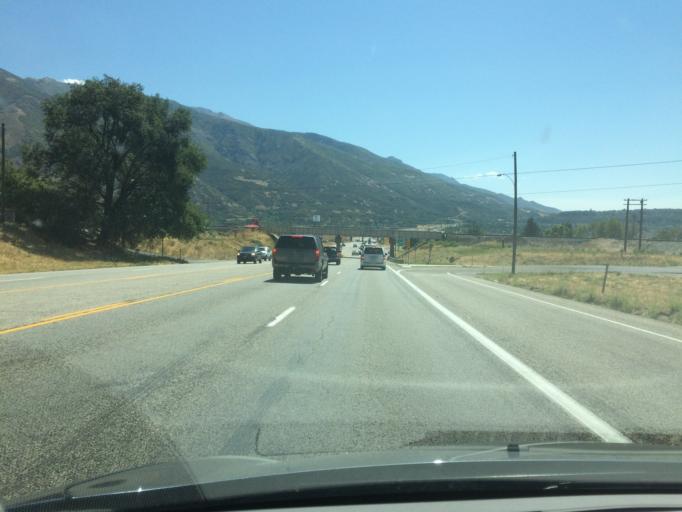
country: US
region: Utah
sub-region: Weber County
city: Uintah
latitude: 41.1426
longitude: -111.9175
